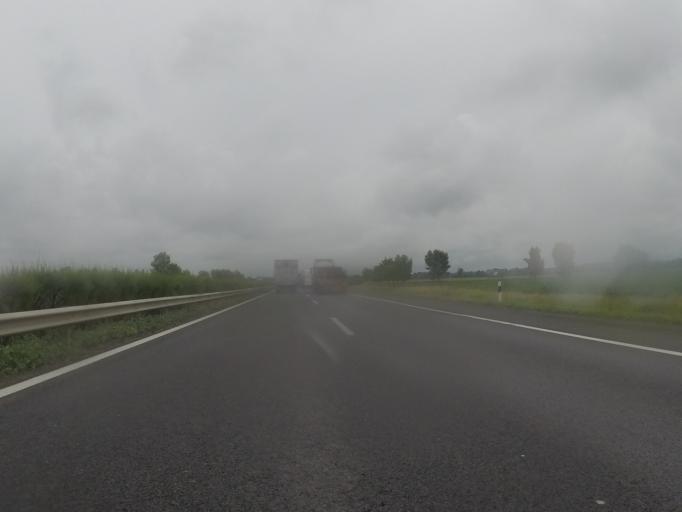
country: HU
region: Gyor-Moson-Sopron
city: Otteveny
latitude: 47.6991
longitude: 17.5019
